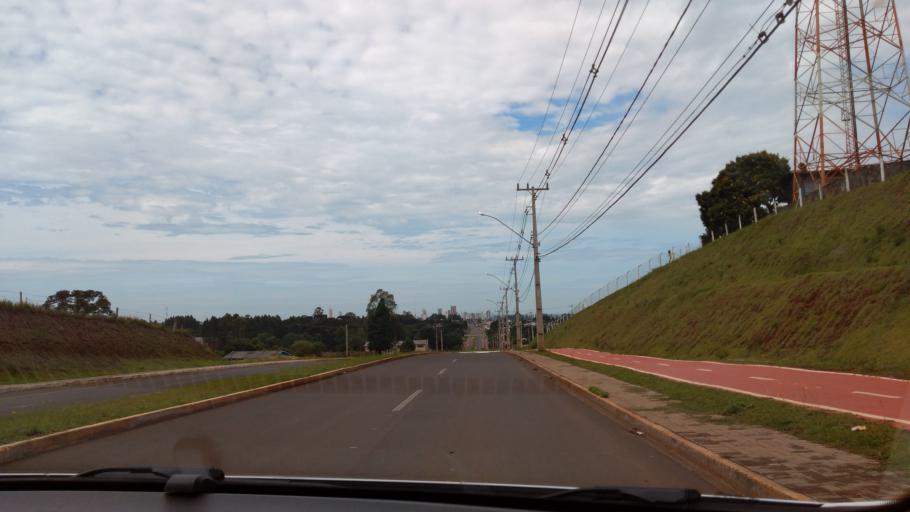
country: BR
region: Parana
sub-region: Guarapuava
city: Guarapuava
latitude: -25.3661
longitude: -51.4348
